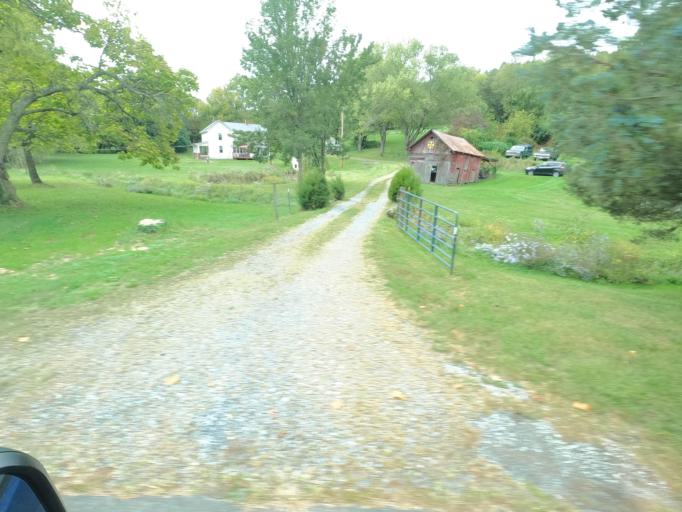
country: US
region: Tennessee
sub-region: Washington County
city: Jonesborough
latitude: 36.2632
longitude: -82.5351
